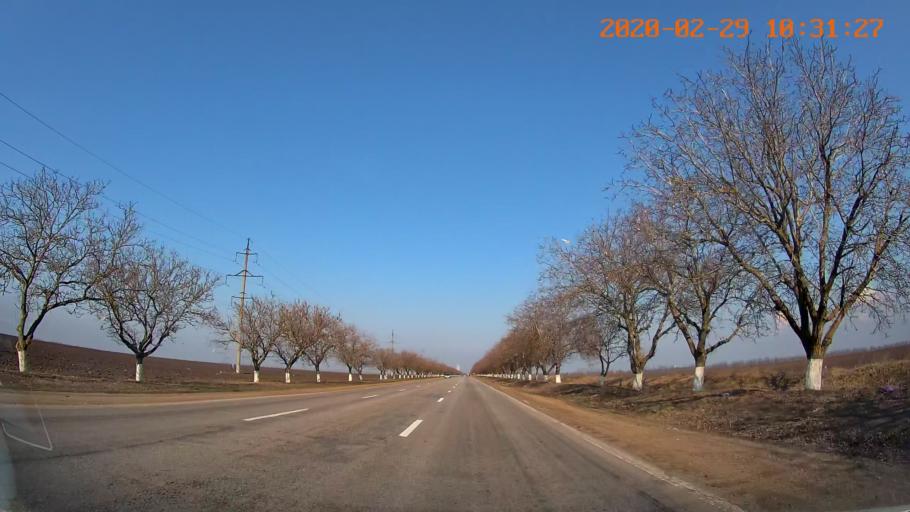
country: MD
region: Telenesti
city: Tiraspolul Nou
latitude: 46.9484
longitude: 29.5640
